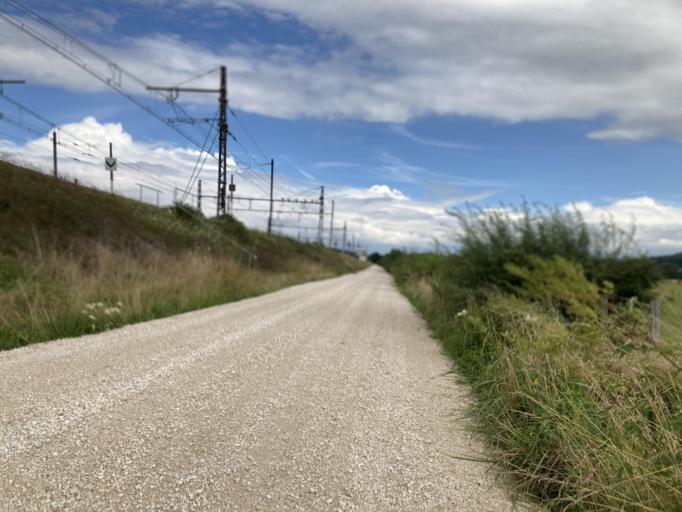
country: FR
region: Bourgogne
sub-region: Departement de la Cote-d'Or
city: Montbard
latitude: 47.6183
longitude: 4.3691
